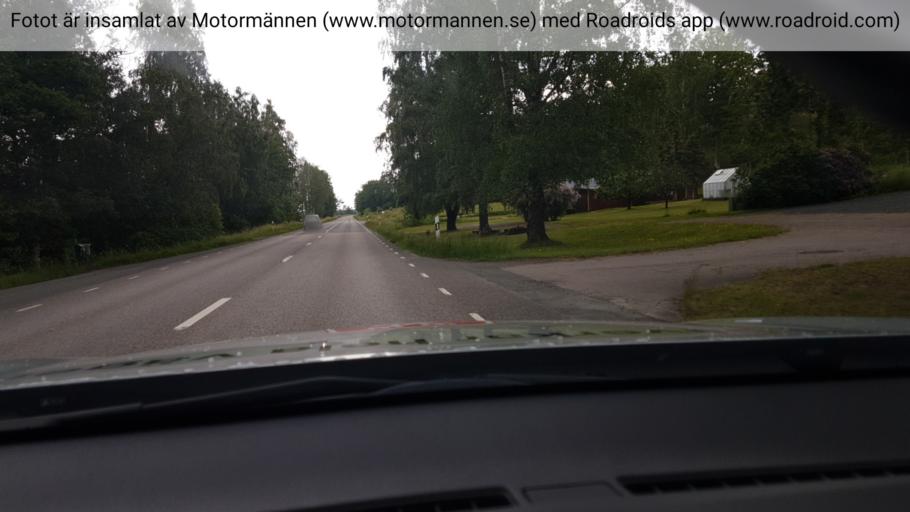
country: SE
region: Vaestra Goetaland
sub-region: Hjo Kommun
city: Hjo
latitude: 58.1565
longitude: 14.2122
